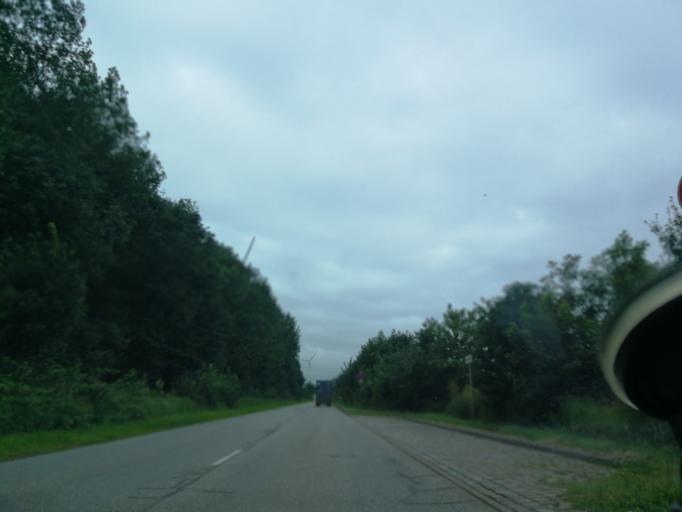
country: DE
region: Hamburg
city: Altona
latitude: 53.5110
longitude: 9.9292
